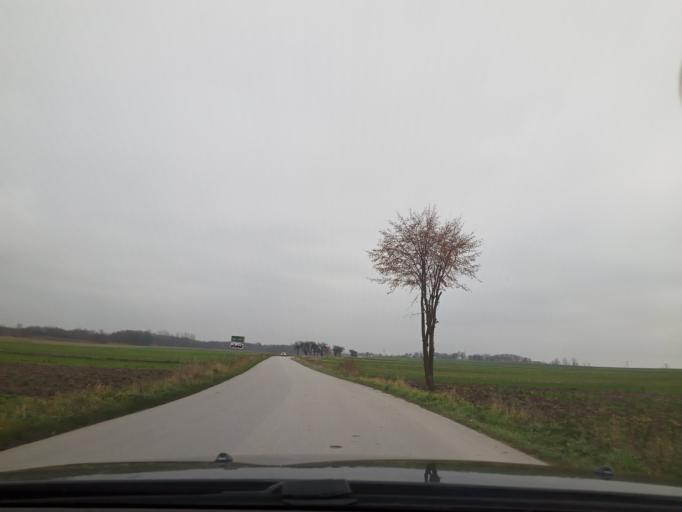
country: PL
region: Swietokrzyskie
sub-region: Powiat jedrzejowski
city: Imielno
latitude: 50.5903
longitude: 20.4268
